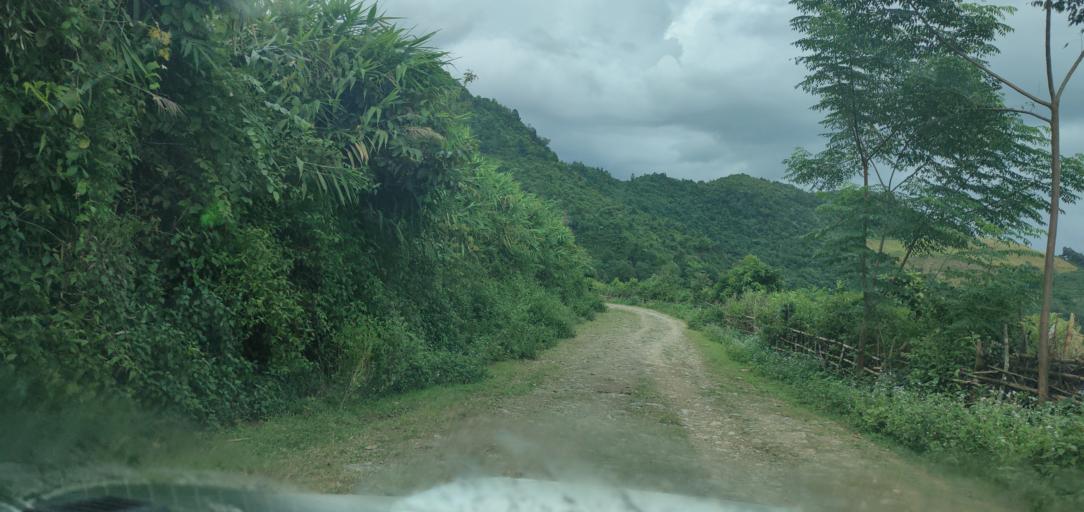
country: LA
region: Phongsali
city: Phongsali
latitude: 21.4461
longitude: 102.3044
